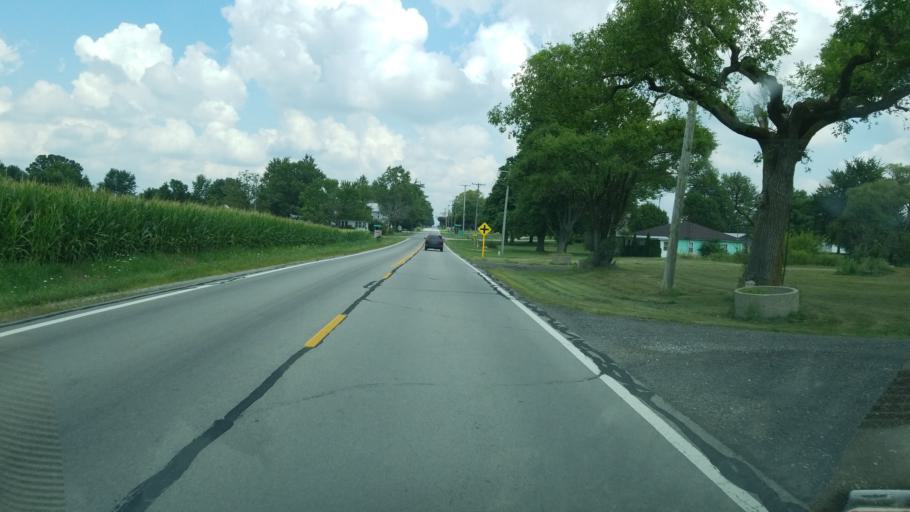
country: US
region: Ohio
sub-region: Crawford County
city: Bucyrus
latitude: 40.6872
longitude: -83.0090
